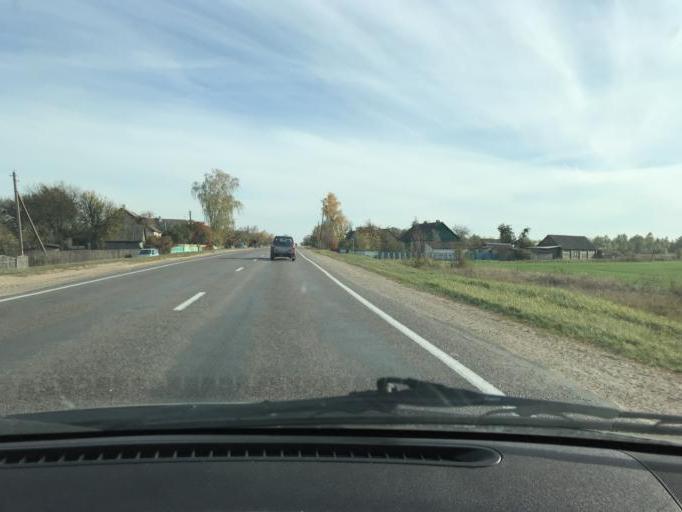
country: BY
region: Brest
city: Lahishyn
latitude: 52.2377
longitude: 26.0077
